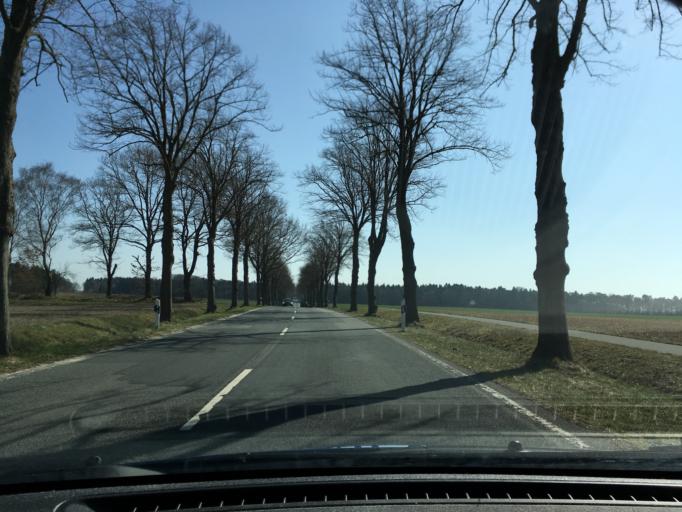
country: DE
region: Lower Saxony
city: Wriedel
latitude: 53.0675
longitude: 10.2849
